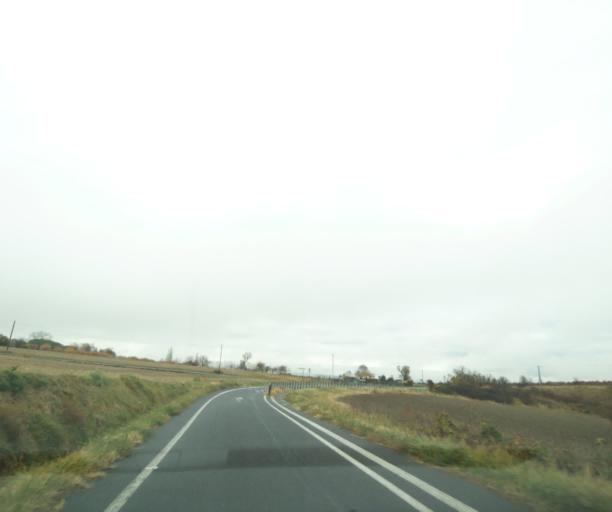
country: FR
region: Auvergne
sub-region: Departement du Puy-de-Dome
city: Cournon-d'Auvergne
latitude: 45.7592
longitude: 3.2070
